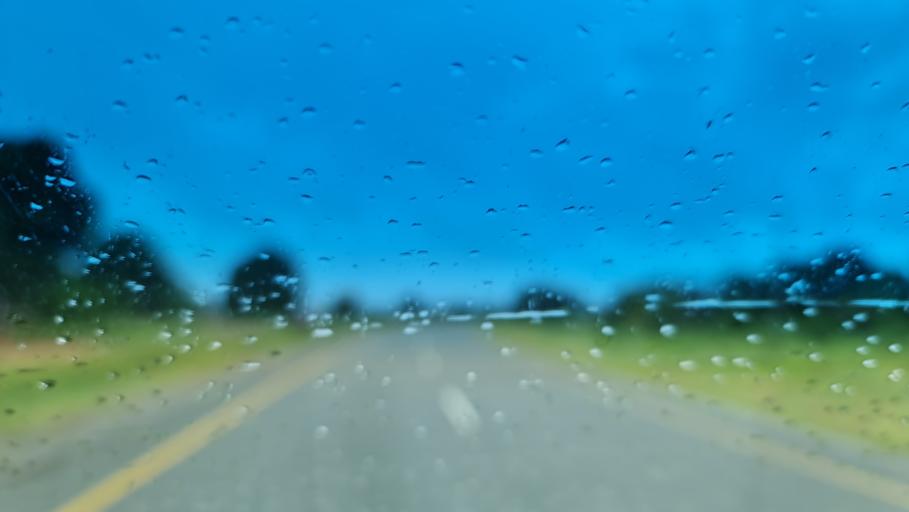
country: MZ
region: Nampula
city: Nampula
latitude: -15.5130
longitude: 39.3344
